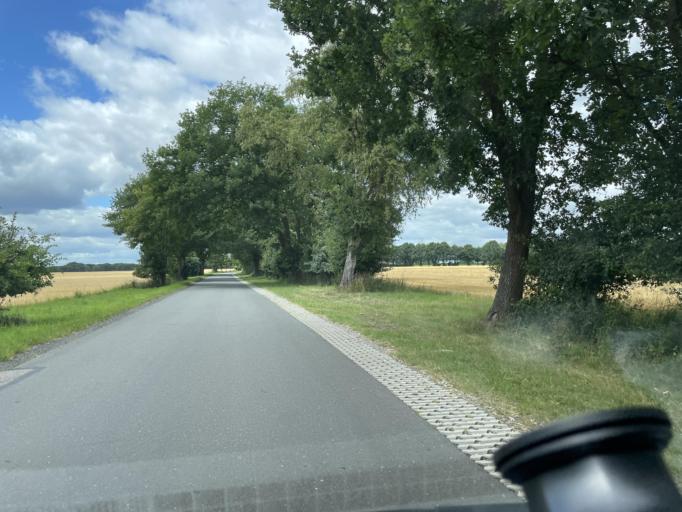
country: DE
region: Lower Saxony
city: Buxtehude
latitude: 53.4496
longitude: 9.7180
